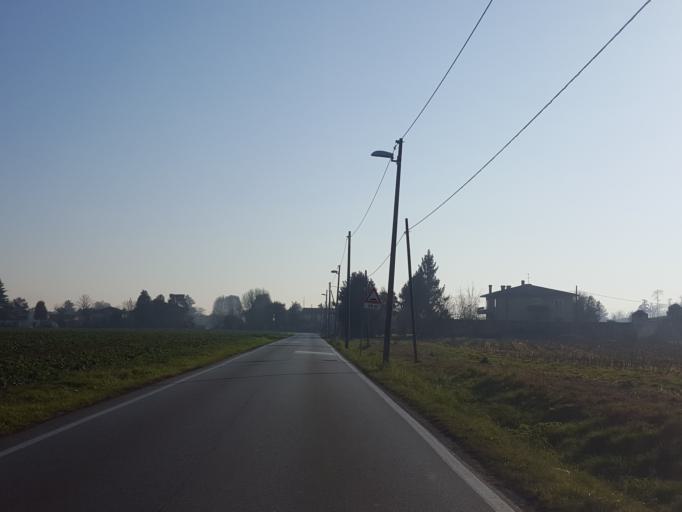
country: IT
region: Veneto
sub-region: Provincia di Vicenza
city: Lisiera
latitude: 45.5648
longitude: 11.5936
